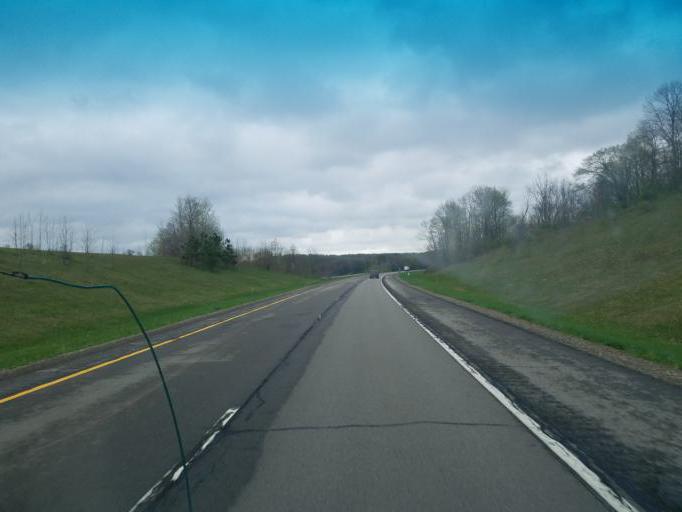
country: US
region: New York
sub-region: Chautauqua County
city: Clymer
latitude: 42.1446
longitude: -79.7064
